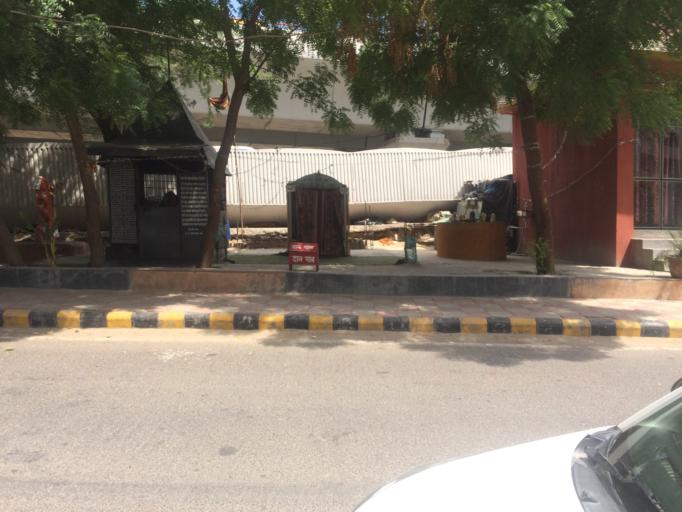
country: IN
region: NCT
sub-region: New Delhi
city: New Delhi
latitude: 28.5848
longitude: 77.2396
